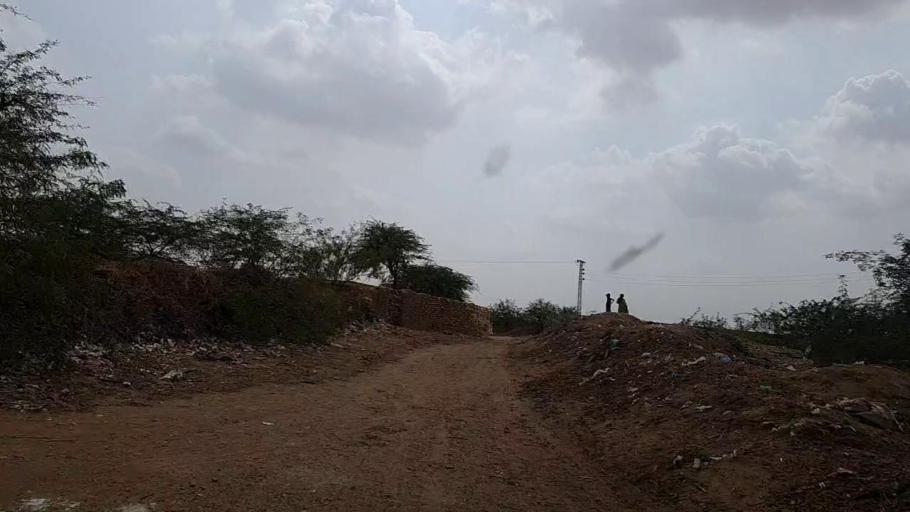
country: PK
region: Sindh
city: Kotri
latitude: 25.2903
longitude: 68.2179
